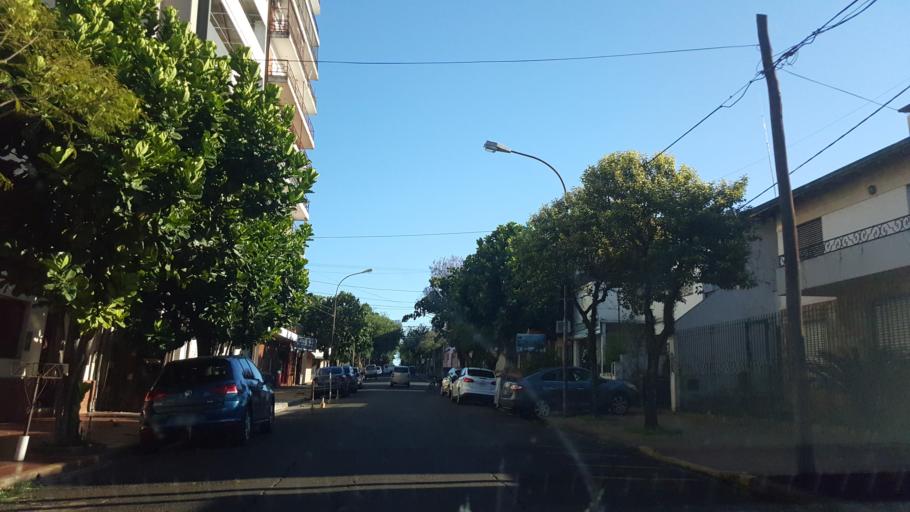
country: AR
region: Misiones
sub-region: Departamento de Capital
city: Posadas
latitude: -27.3693
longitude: -55.9003
